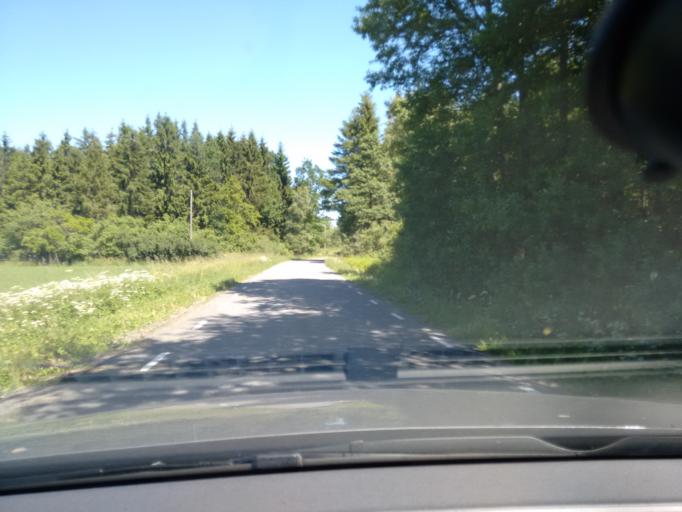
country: SE
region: Skane
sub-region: Kristianstads Kommun
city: Degeberga
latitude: 55.7804
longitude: 14.0551
